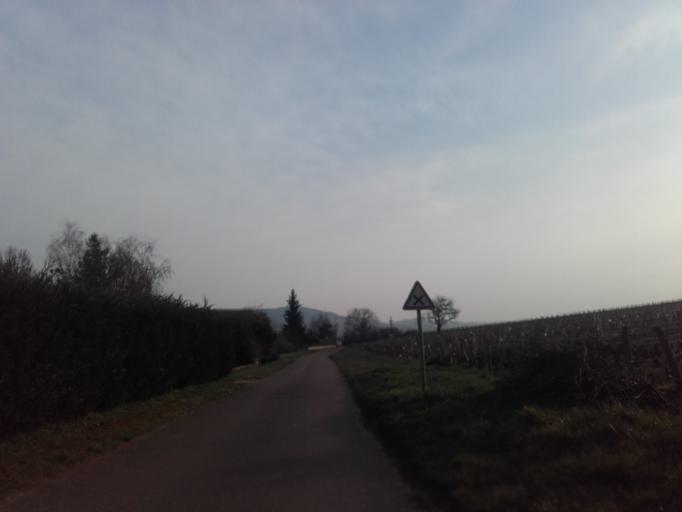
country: FR
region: Bourgogne
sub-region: Departement de la Cote-d'Or
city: Nolay
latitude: 46.9112
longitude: 4.6813
